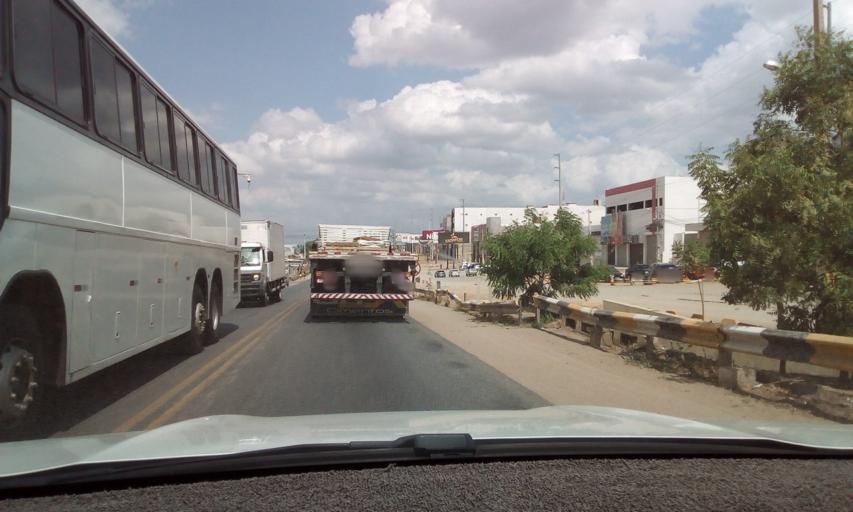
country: BR
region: Pernambuco
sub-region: Toritama
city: Toritama
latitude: -8.0073
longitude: -36.0655
